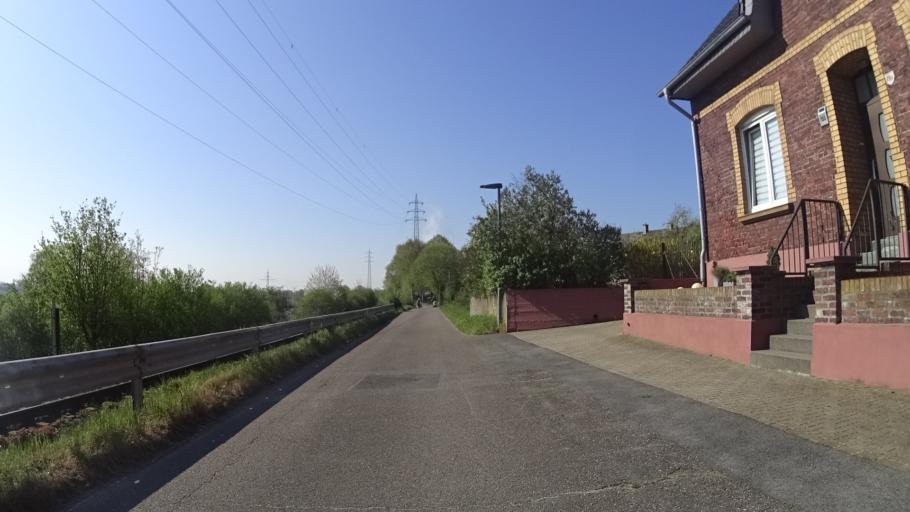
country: DE
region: North Rhine-Westphalia
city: Rheinberg
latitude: 51.5687
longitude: 6.5888
